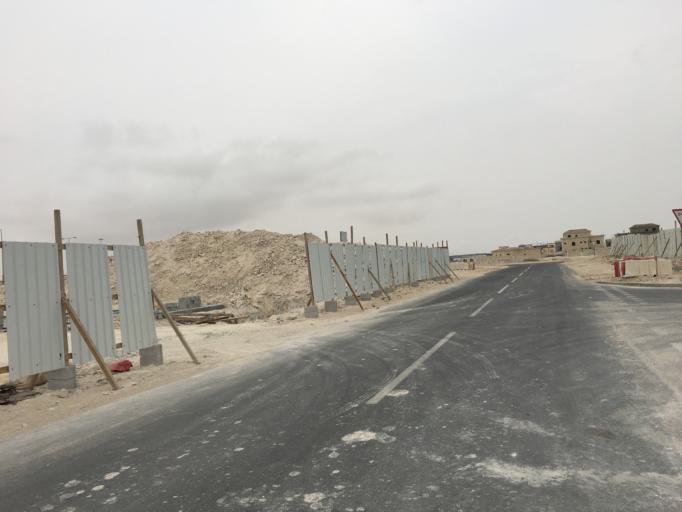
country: QA
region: Baladiyat Umm Salal
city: Umm Salal Muhammad
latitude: 25.3914
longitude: 51.4368
